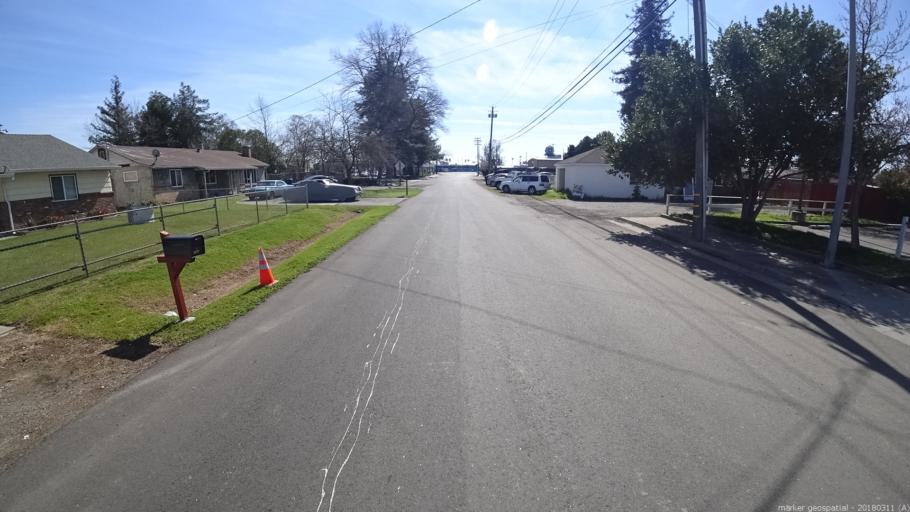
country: US
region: California
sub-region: Sacramento County
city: Florin
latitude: 38.4978
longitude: -121.3960
